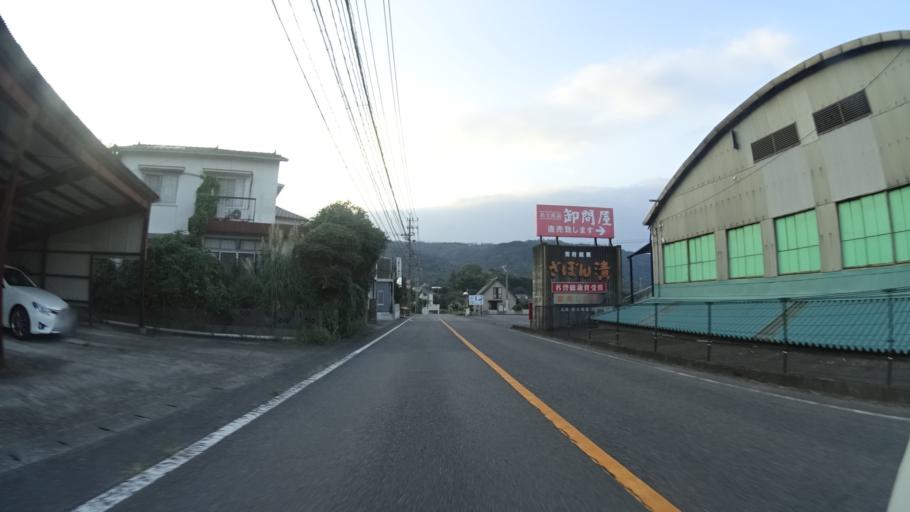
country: JP
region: Oita
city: Beppu
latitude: 33.3216
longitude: 131.4795
